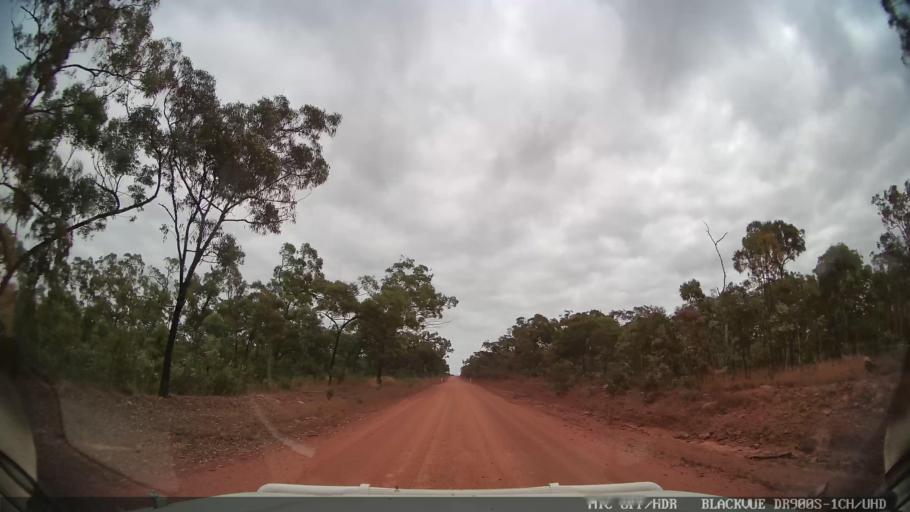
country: AU
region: Queensland
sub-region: Cook
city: Cooktown
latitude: -15.2657
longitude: 144.9495
